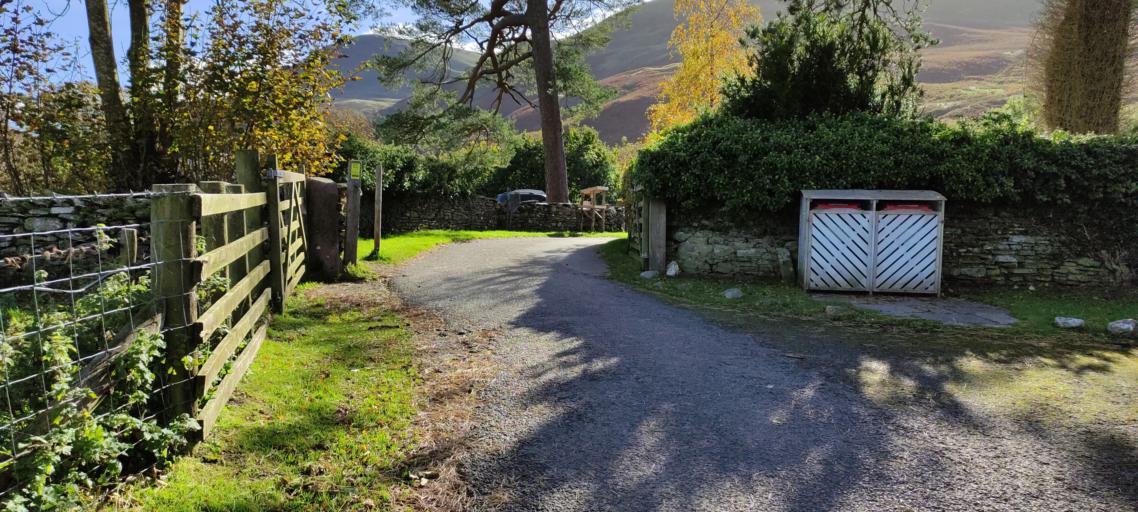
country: GB
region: England
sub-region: Cumbria
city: Cockermouth
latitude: 54.5876
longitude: -3.3702
